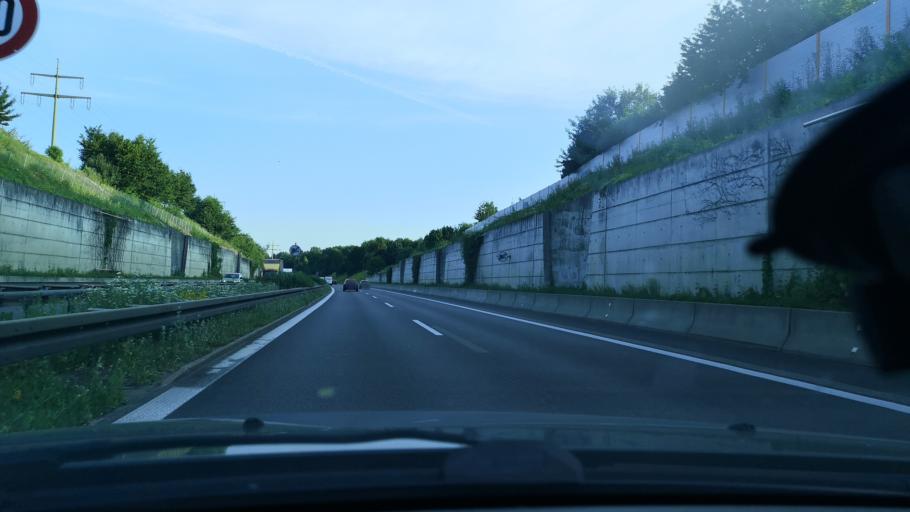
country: DE
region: Baden-Wuerttemberg
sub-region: Regierungsbezirk Stuttgart
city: Eislingen
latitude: 48.6862
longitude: 9.7001
